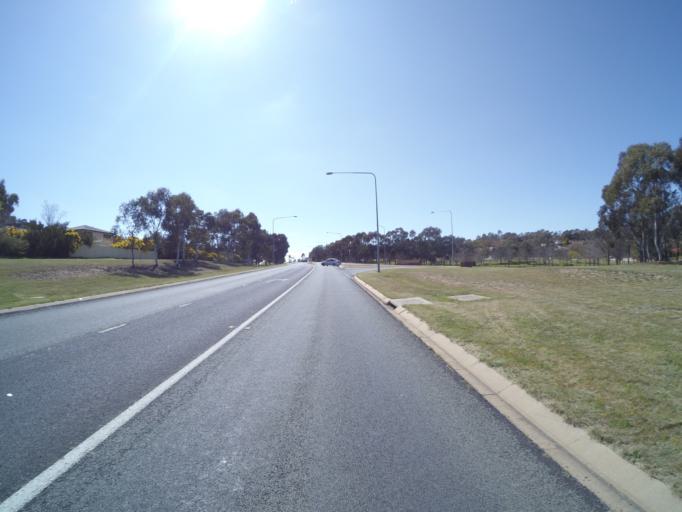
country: AU
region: Australian Capital Territory
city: Macarthur
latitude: -35.4428
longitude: 149.0851
